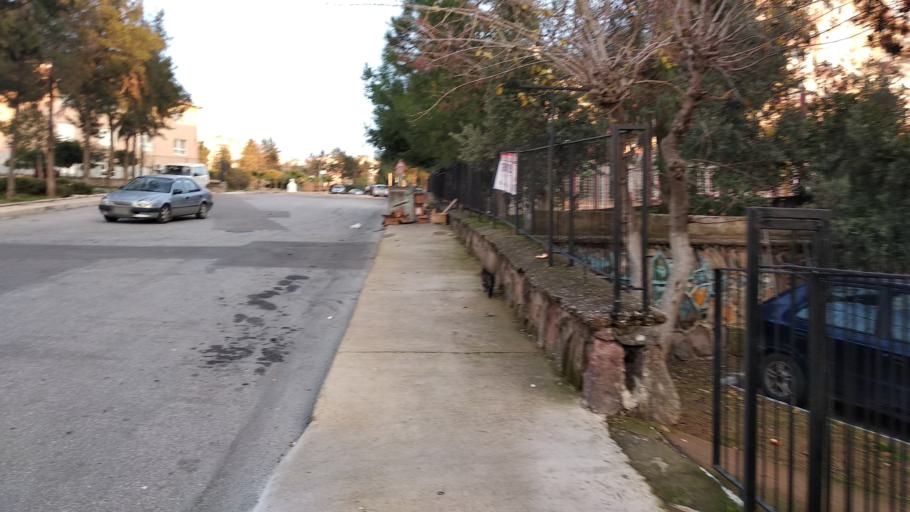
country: TR
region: Izmir
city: Karsiyaka
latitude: 38.4959
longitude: 27.0857
